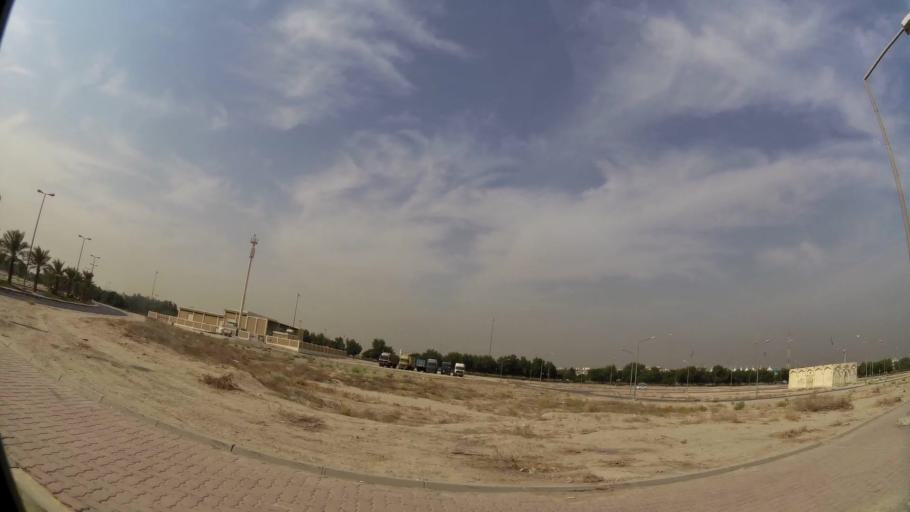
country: KW
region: Al Farwaniyah
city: Janub as Surrah
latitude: 29.2796
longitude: 47.9886
